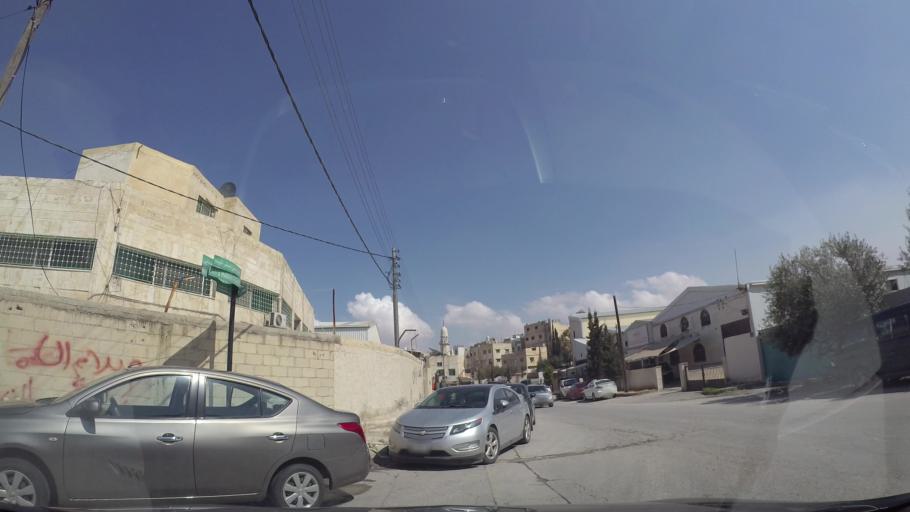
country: JO
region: Zarqa
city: Russeifa
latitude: 31.9885
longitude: 36.0147
